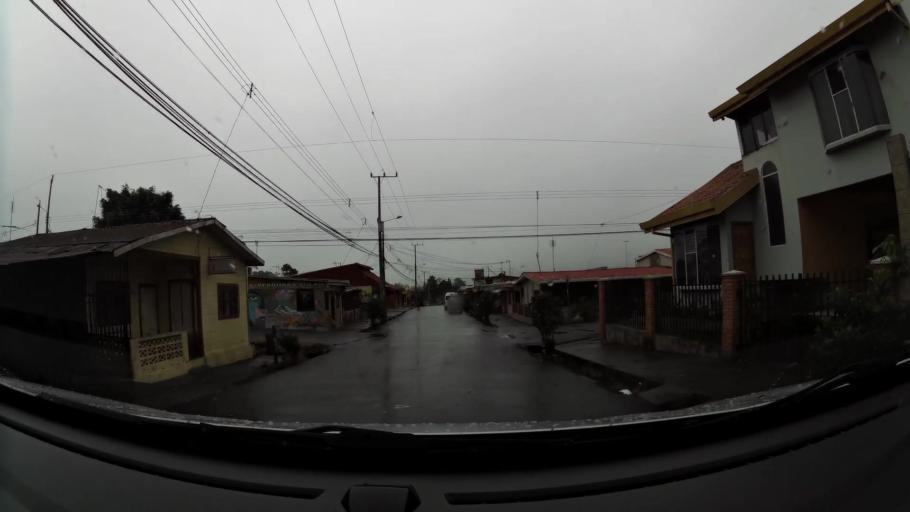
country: CR
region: Cartago
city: Paraiso
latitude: 9.8388
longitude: -83.8632
